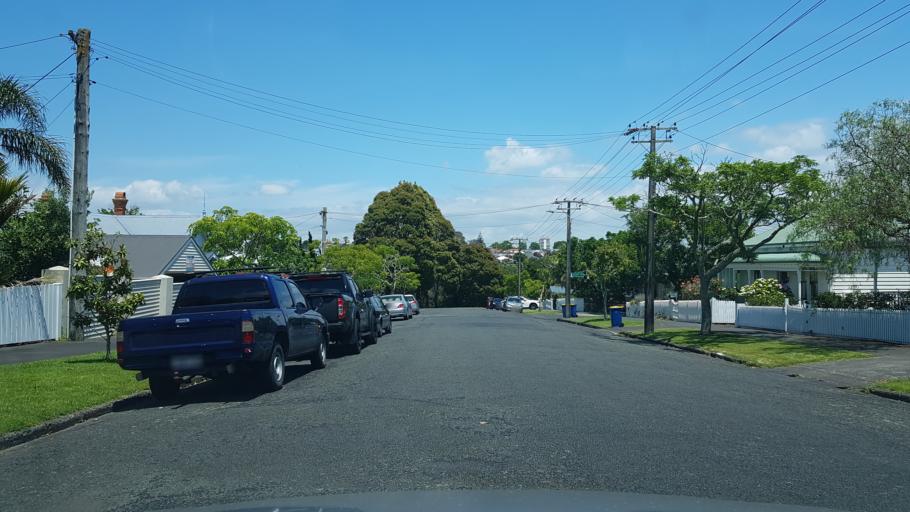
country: NZ
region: Auckland
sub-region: Auckland
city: North Shore
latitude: -36.8236
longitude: 174.7923
